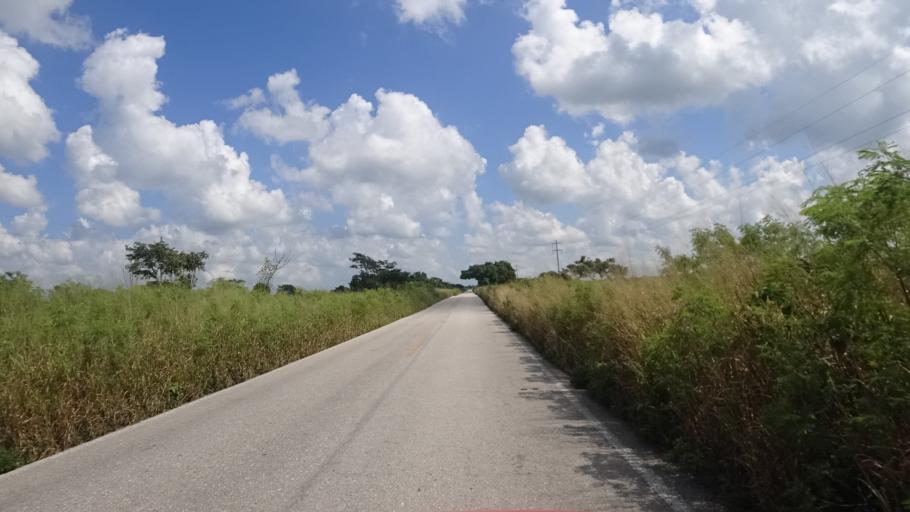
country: MX
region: Yucatan
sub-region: Panaba
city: Loche
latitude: 21.3547
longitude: -88.1491
